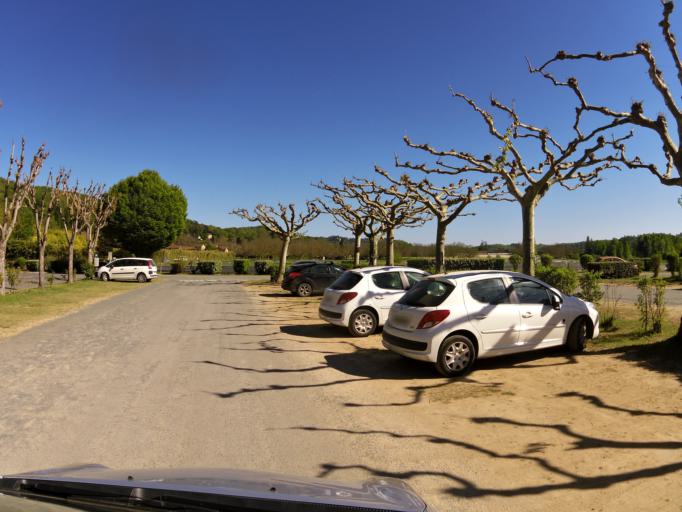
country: FR
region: Aquitaine
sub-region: Departement de la Dordogne
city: Cenac-et-Saint-Julien
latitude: 44.8245
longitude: 1.1844
